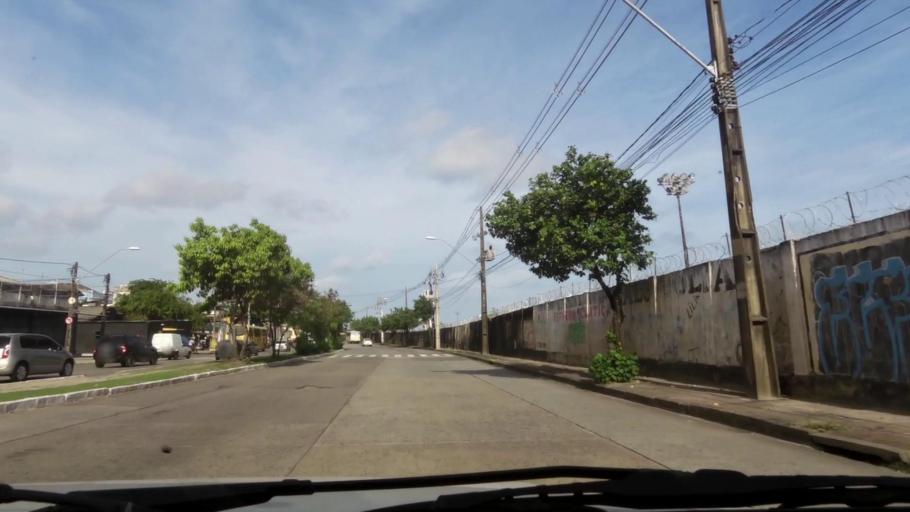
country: BR
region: Pernambuco
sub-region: Recife
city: Recife
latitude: -8.0738
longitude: -34.8865
